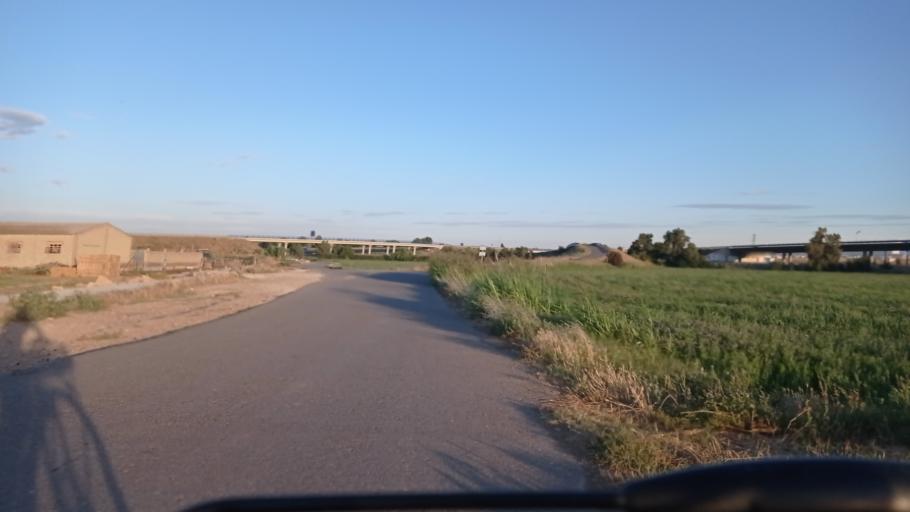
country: ES
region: Aragon
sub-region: Provincia de Zaragoza
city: Almozara
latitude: 41.6800
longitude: -0.9318
